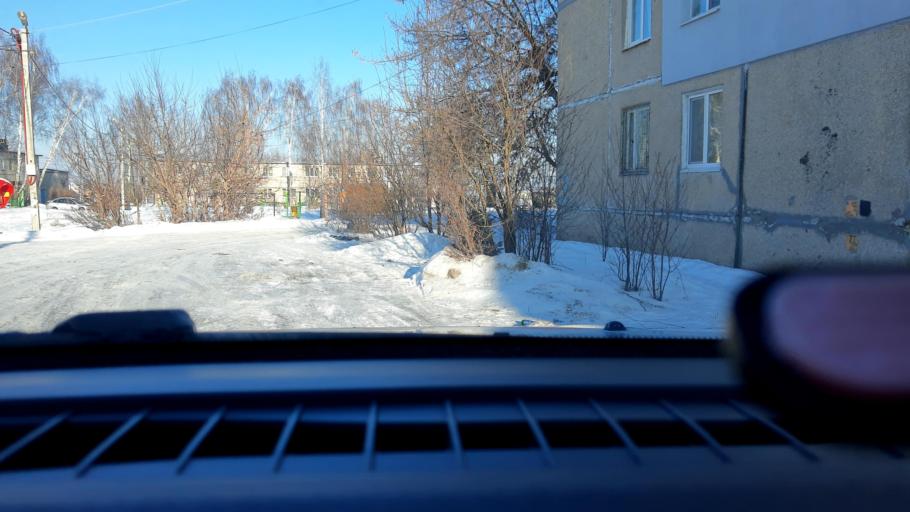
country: RU
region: Nizjnij Novgorod
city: Burevestnik
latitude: 56.1402
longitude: 43.9222
